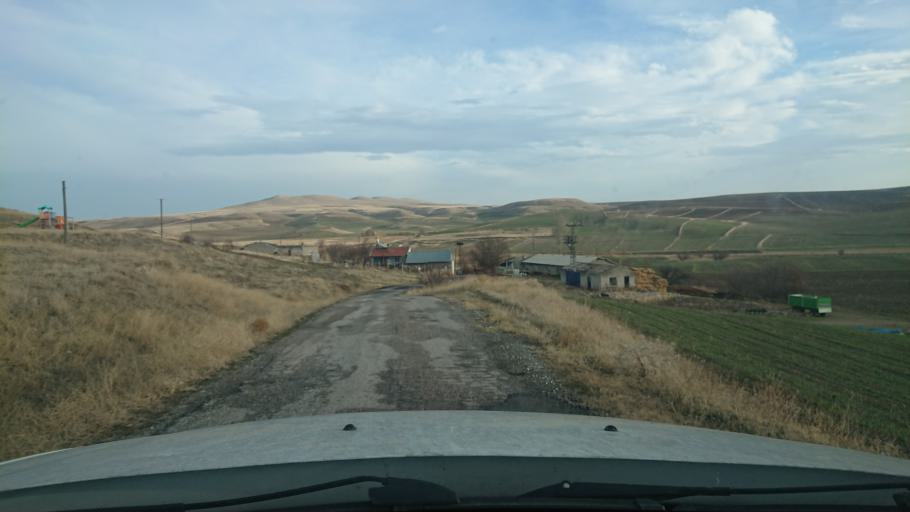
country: TR
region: Aksaray
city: Acipinar
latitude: 38.6746
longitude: 33.8654
